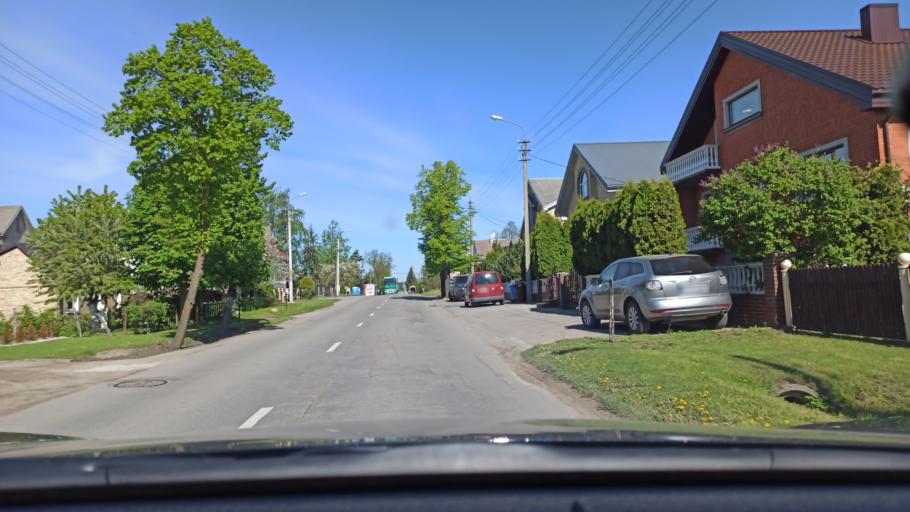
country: LT
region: Siauliu apskritis
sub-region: Siauliai
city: Siauliai
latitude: 55.9611
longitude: 23.2974
